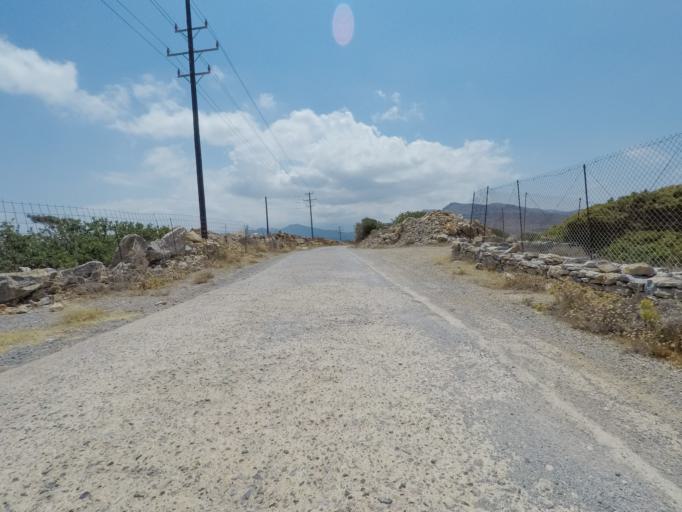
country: GR
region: Crete
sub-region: Nomos Lasithiou
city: Elounda
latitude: 35.3148
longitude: 25.7433
